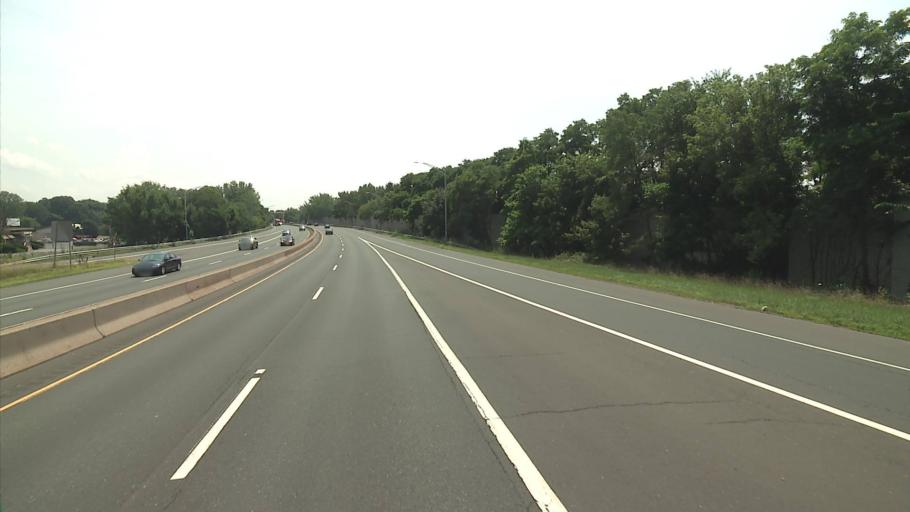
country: US
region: Connecticut
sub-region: Hartford County
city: South Windsor
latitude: 41.8157
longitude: -72.6530
